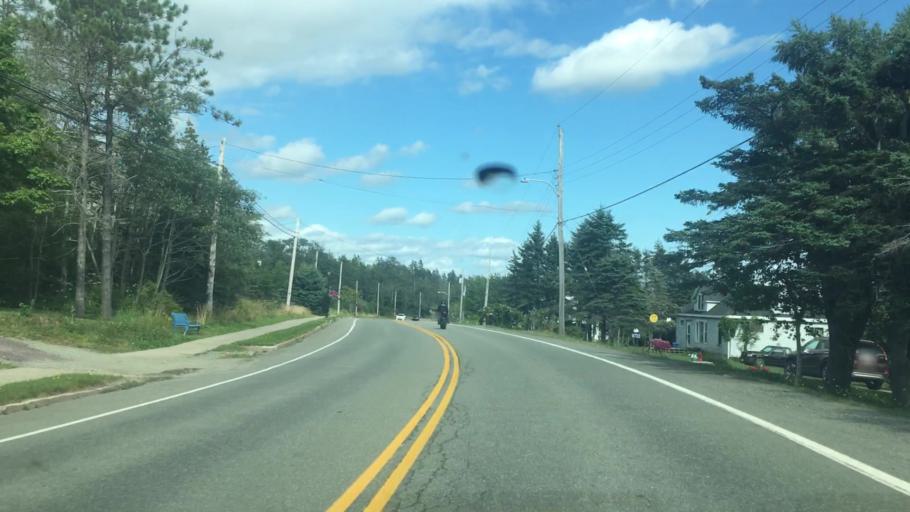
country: CA
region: Nova Scotia
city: Princeville
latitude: 45.6545
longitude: -60.8901
